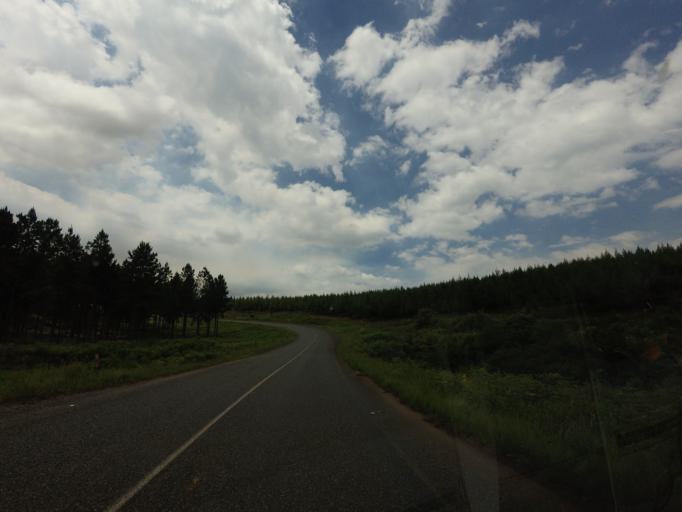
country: ZA
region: Mpumalanga
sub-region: Ehlanzeni District
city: Graksop
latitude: -24.9650
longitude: 30.8123
